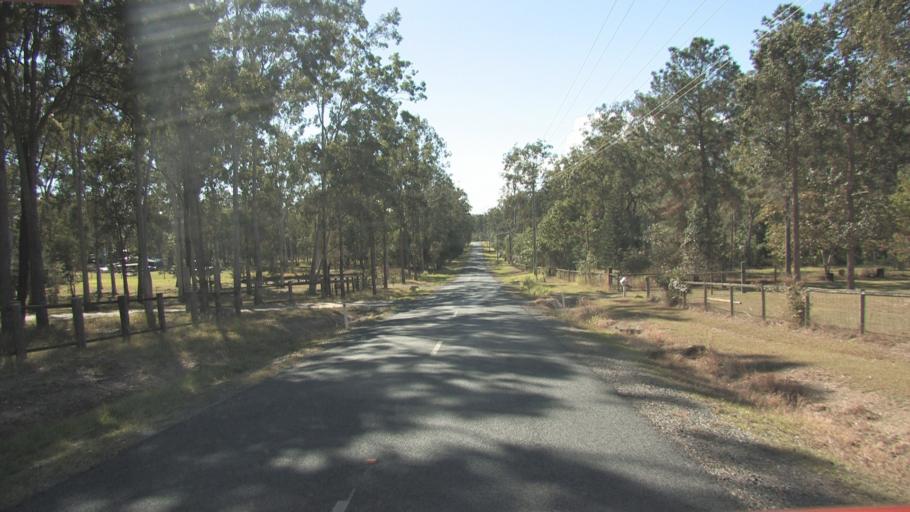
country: AU
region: Queensland
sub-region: Logan
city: Chambers Flat
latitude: -27.8088
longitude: 153.0722
